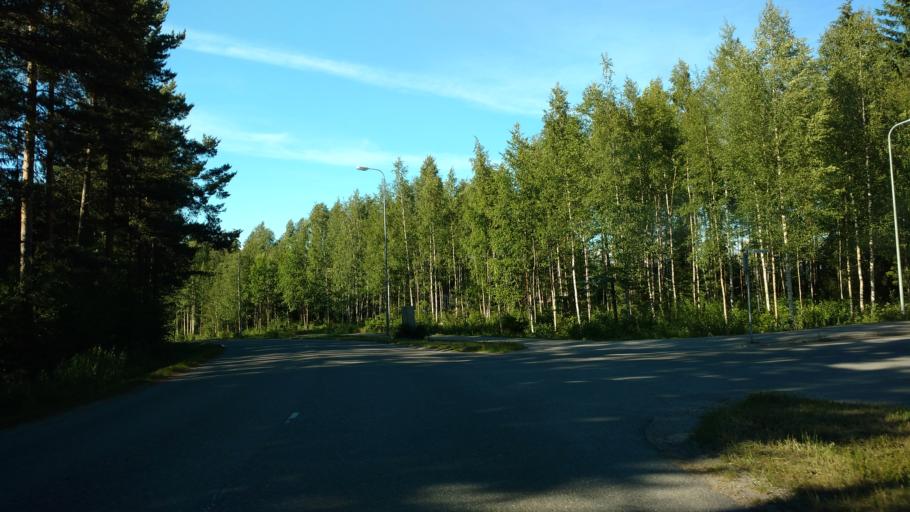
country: FI
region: Varsinais-Suomi
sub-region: Salo
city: Salo
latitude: 60.4055
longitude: 23.1922
